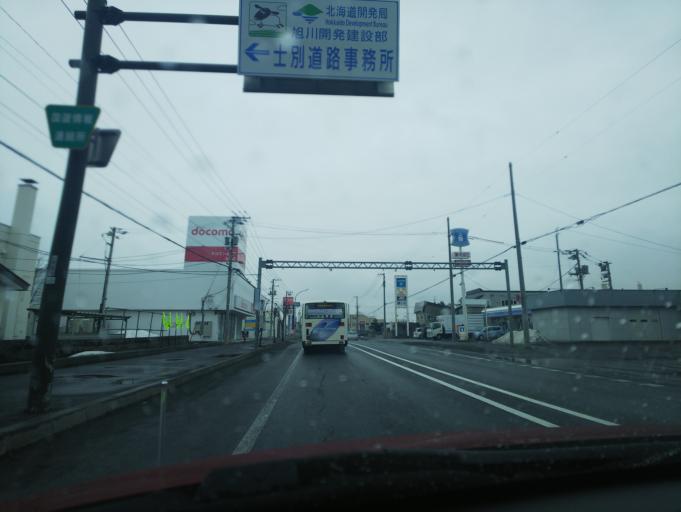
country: JP
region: Hokkaido
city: Nayoro
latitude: 44.1670
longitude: 142.3950
